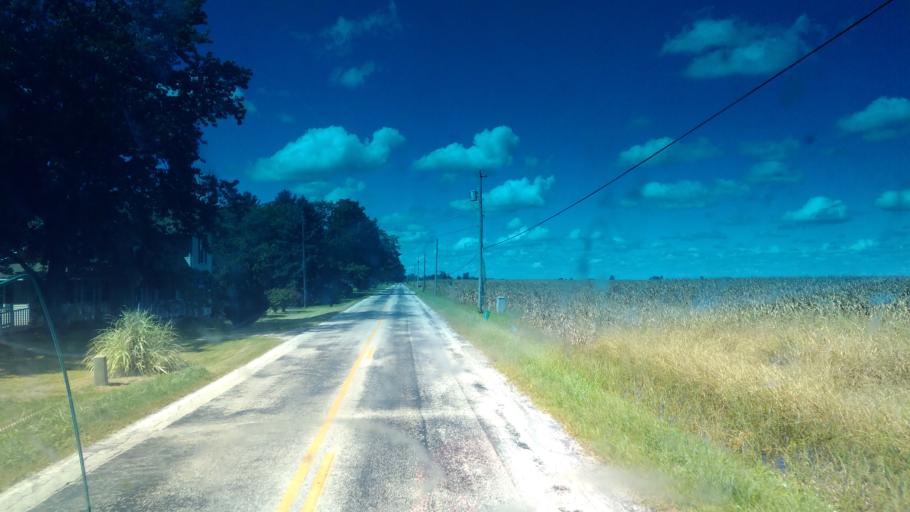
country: US
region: Ohio
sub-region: Madison County
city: West Jefferson
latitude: 39.9893
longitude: -83.3378
